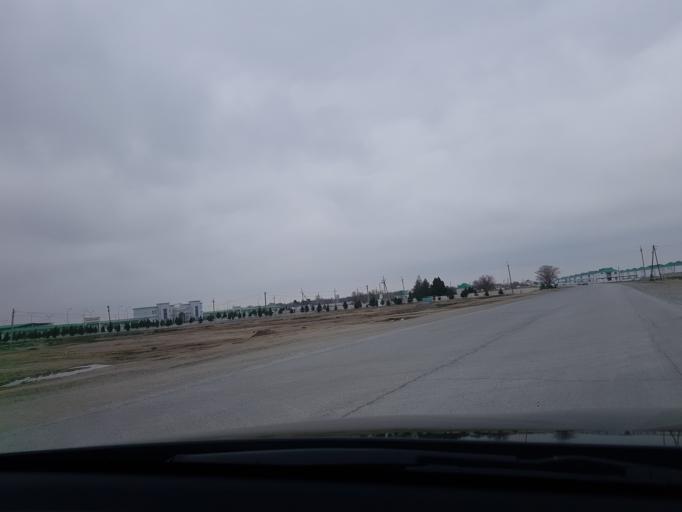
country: TM
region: Ahal
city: Arcabil
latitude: 38.1315
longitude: 57.9455
